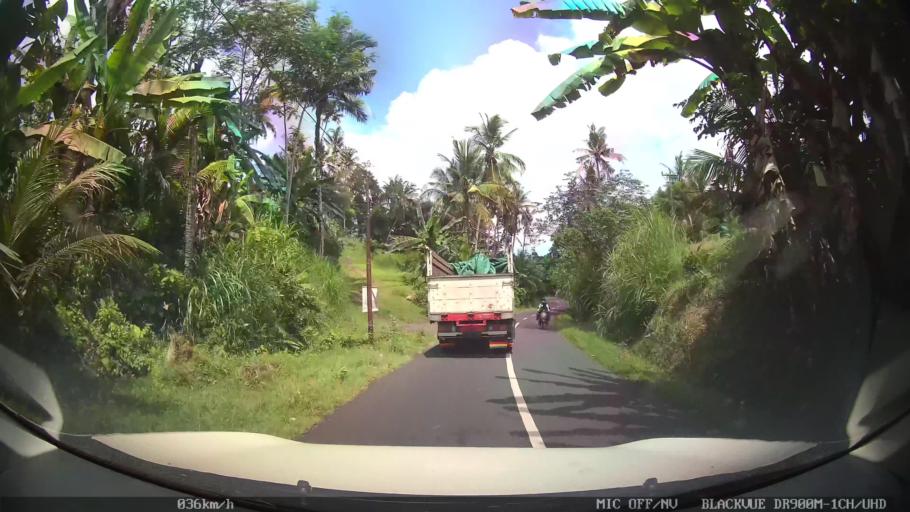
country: ID
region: Bali
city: Banjar Kelodan
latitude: -8.5170
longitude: 115.3650
